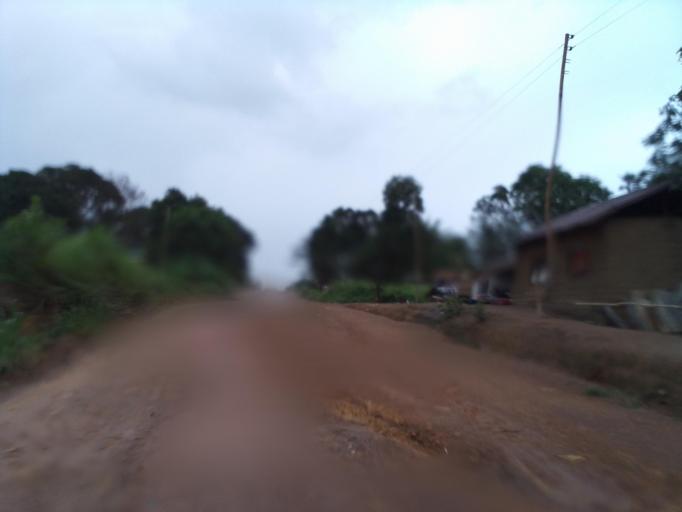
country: SL
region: Eastern Province
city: Kenema
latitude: 7.8768
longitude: -11.1647
